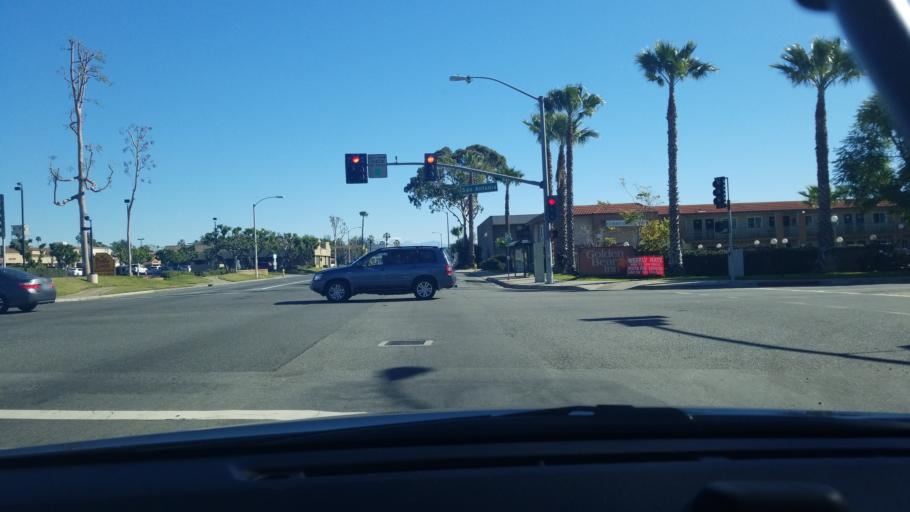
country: US
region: California
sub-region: San Bernardino County
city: Ontario
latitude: 34.0633
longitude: -117.6608
